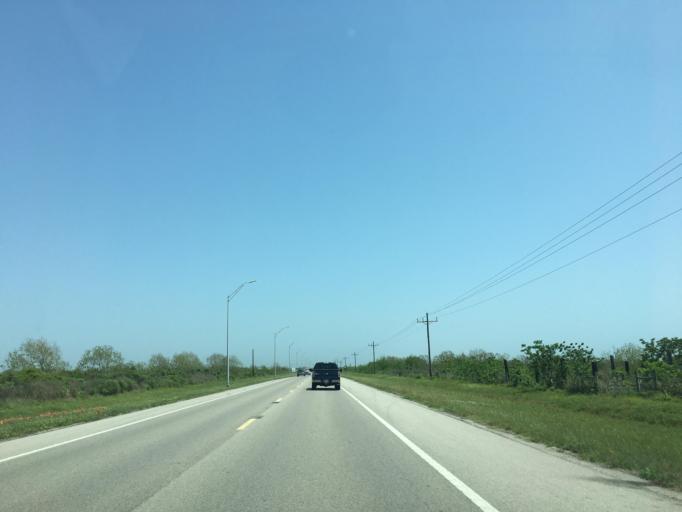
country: US
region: Texas
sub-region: Galveston County
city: Galveston
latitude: 29.3878
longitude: -94.7364
